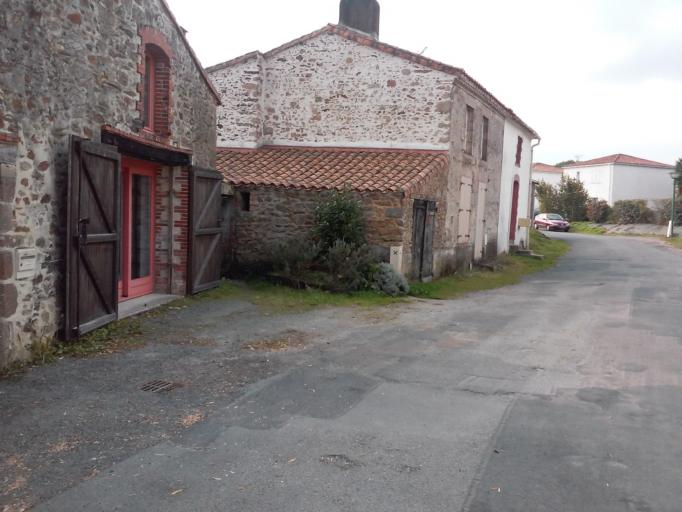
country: FR
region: Pays de la Loire
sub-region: Departement de la Vendee
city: La Chaize-le-Vicomte
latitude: 46.6717
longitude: -1.2957
